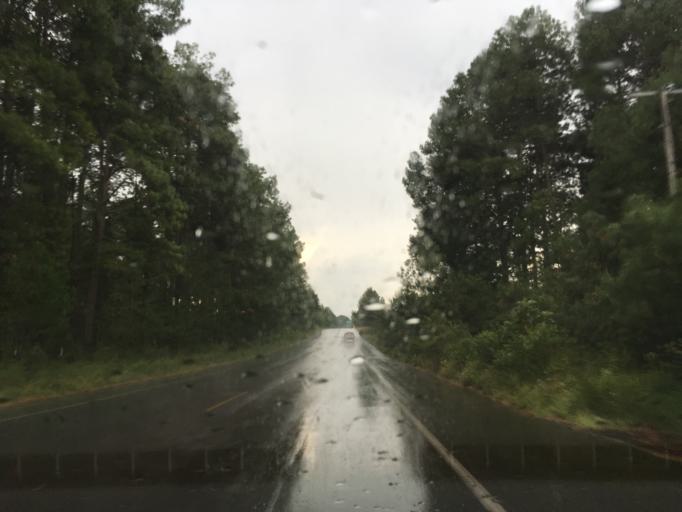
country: MX
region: Michoacan
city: Angahuan
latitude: 19.5263
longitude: -102.1886
